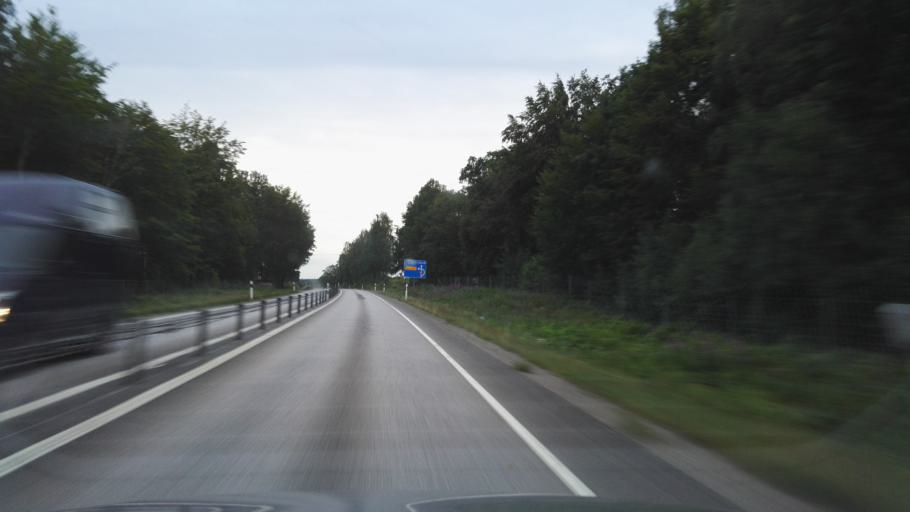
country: SE
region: Kronoberg
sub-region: Vaxjo Kommun
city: Rottne
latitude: 56.9853
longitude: 14.9881
